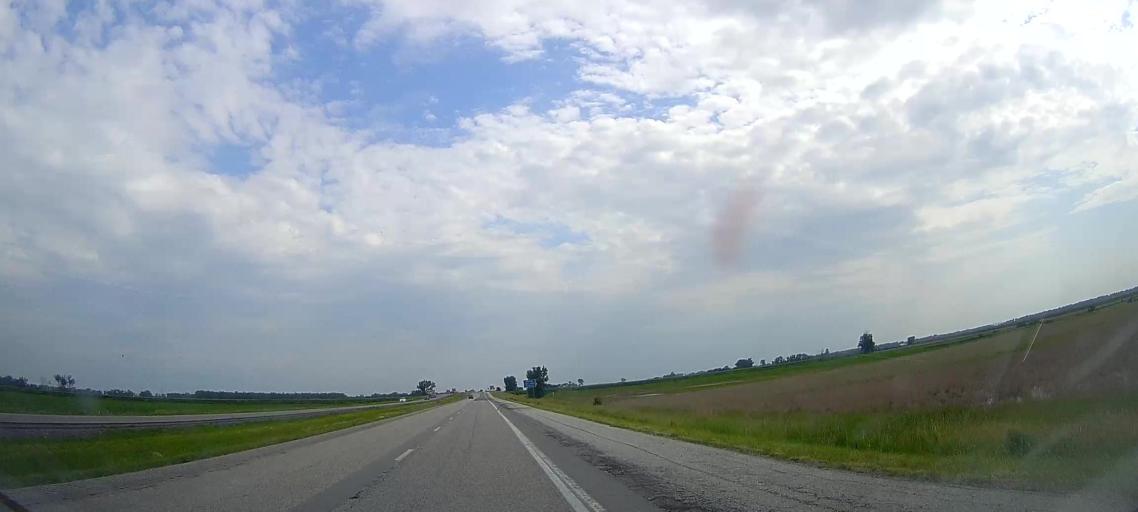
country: US
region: Nebraska
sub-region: Burt County
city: Tekamah
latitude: 41.7558
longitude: -96.0459
